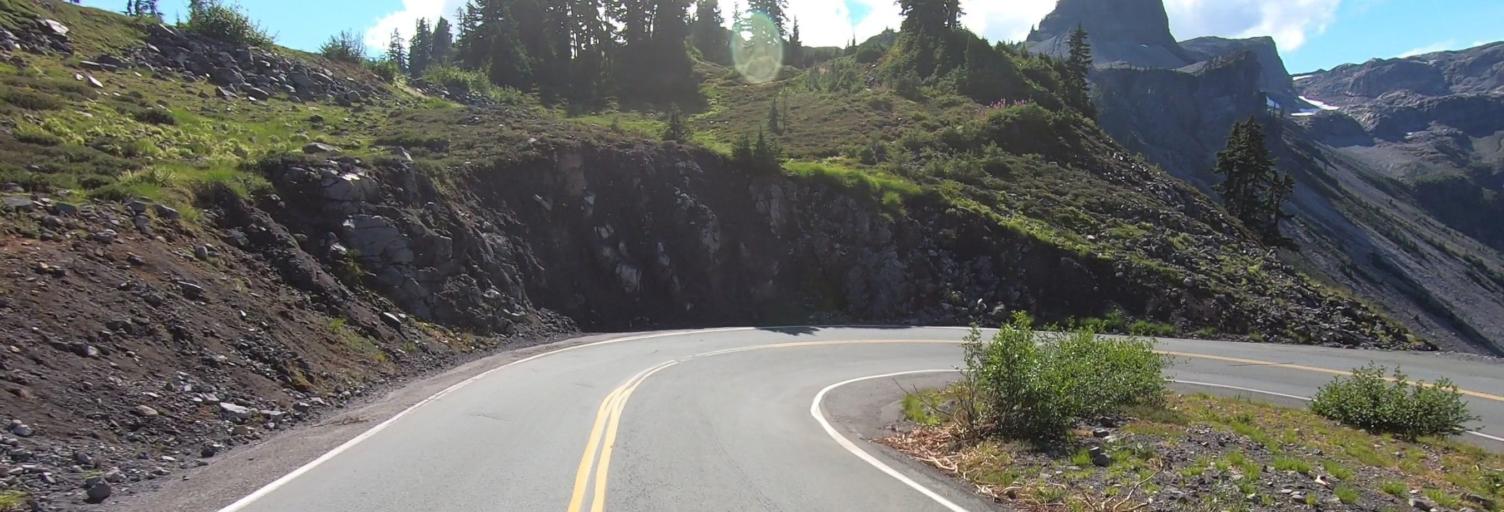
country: CA
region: British Columbia
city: Agassiz
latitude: 48.8512
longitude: -121.6862
